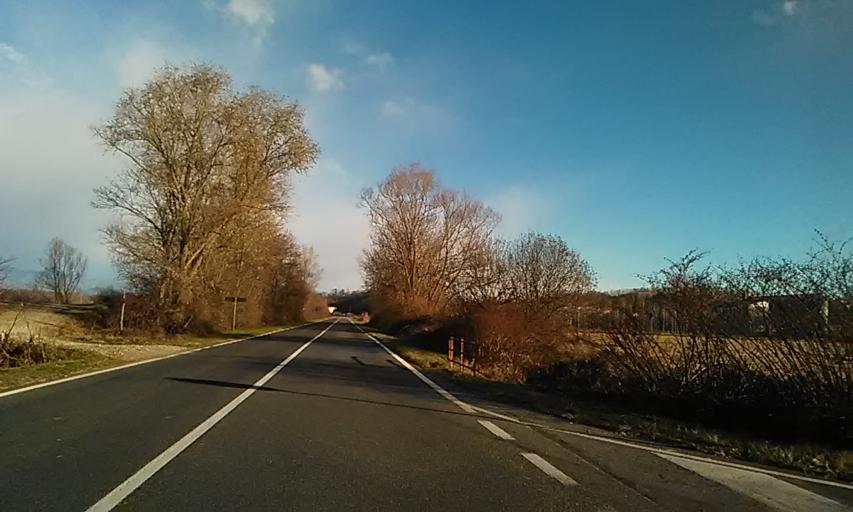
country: IT
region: Piedmont
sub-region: Provincia di Vercelli
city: Buronzo
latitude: 45.4809
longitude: 8.2611
